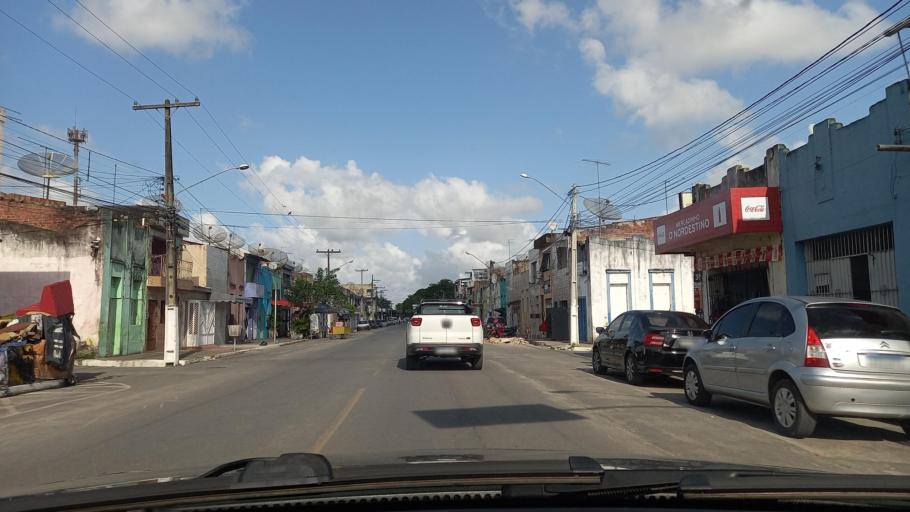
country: BR
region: Pernambuco
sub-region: Goiana
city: Goiana
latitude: -7.5601
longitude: -34.9938
